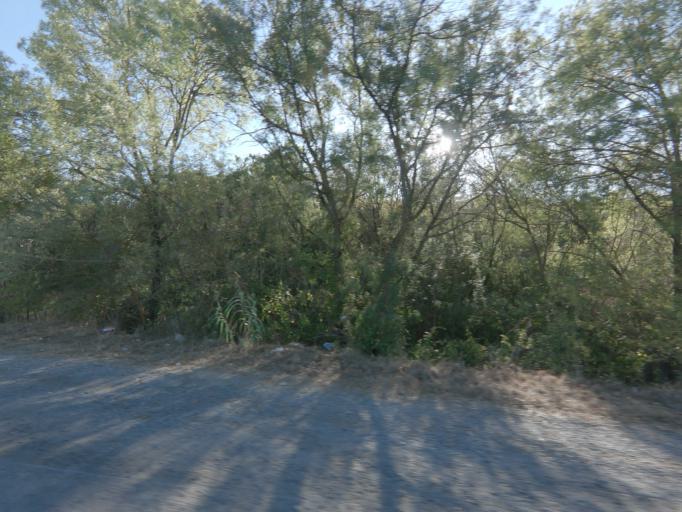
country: PT
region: Setubal
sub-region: Palmela
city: Quinta do Anjo
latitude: 38.5118
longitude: -8.9715
